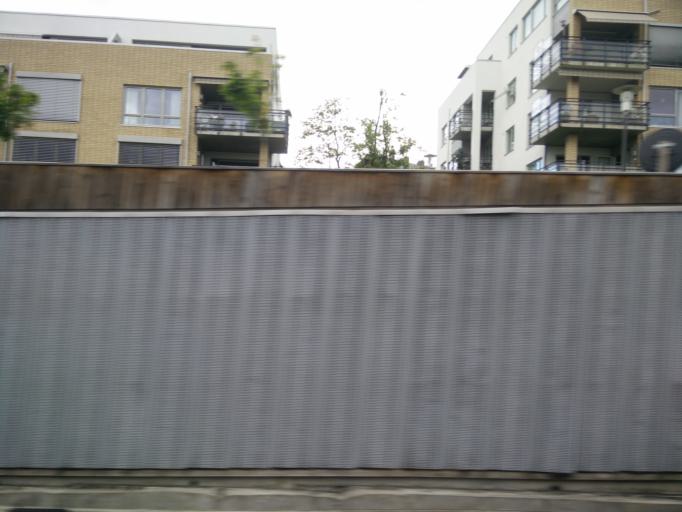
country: NO
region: Akershus
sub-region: Baerum
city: Lysaker
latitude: 59.9481
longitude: 10.6408
